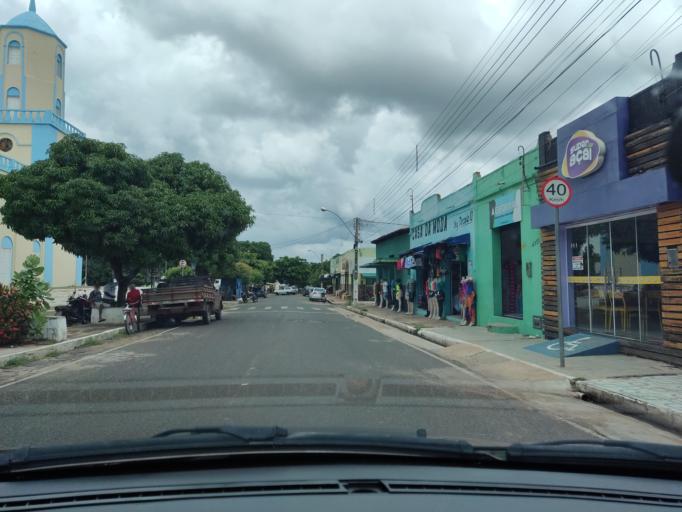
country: BR
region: Piaui
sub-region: Valenca Do Piaui
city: Valenca do Piaui
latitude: -6.4025
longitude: -41.7409
